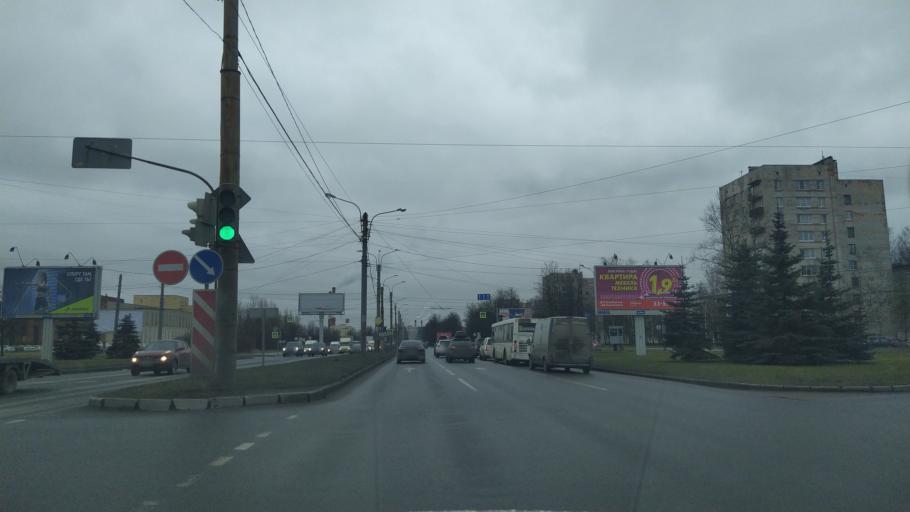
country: RU
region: Leningrad
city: Akademicheskoe
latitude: 60.0041
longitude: 30.4360
